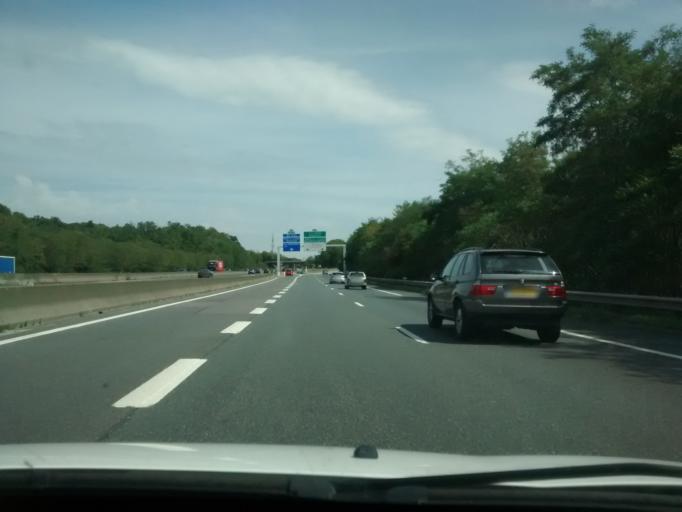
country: FR
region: Ile-de-France
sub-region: Departement de l'Essonne
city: Les Ulis
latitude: 48.6650
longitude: 2.1902
